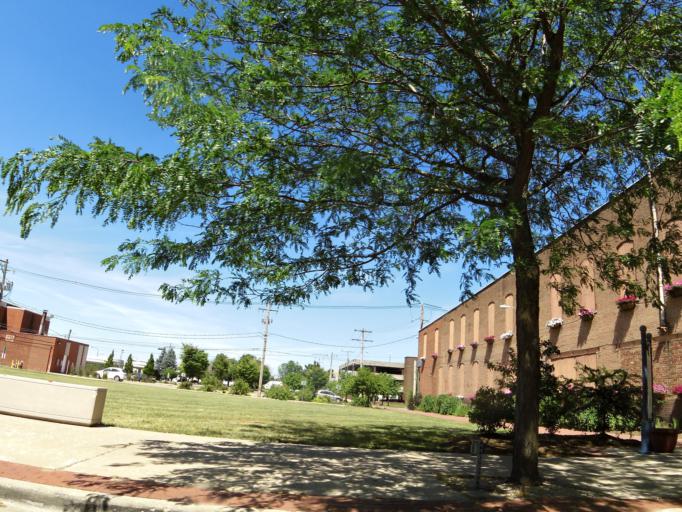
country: US
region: Illinois
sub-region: Vermilion County
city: Danville
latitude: 40.1254
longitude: -87.6300
